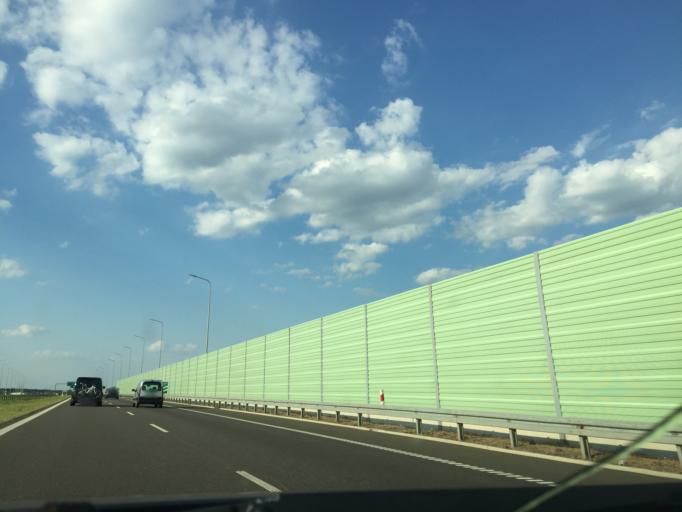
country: PL
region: Masovian Voivodeship
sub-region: Powiat radomski
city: Wolanow
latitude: 51.3811
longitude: 21.0211
